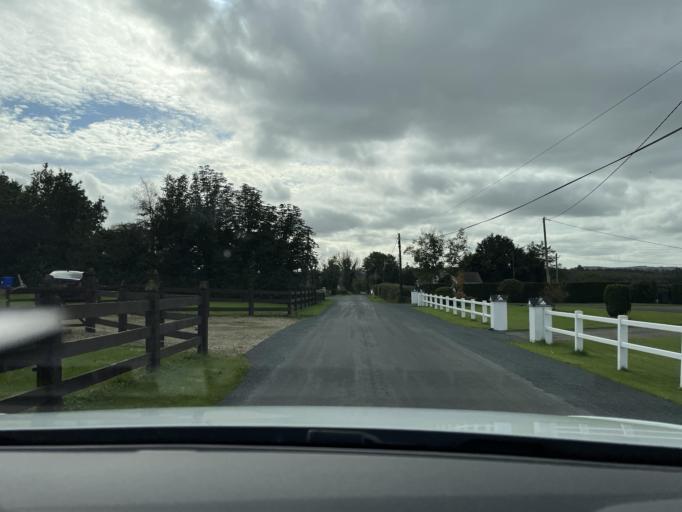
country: IE
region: Connaught
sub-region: County Leitrim
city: Carrick-on-Shannon
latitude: 53.9651
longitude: -8.0841
